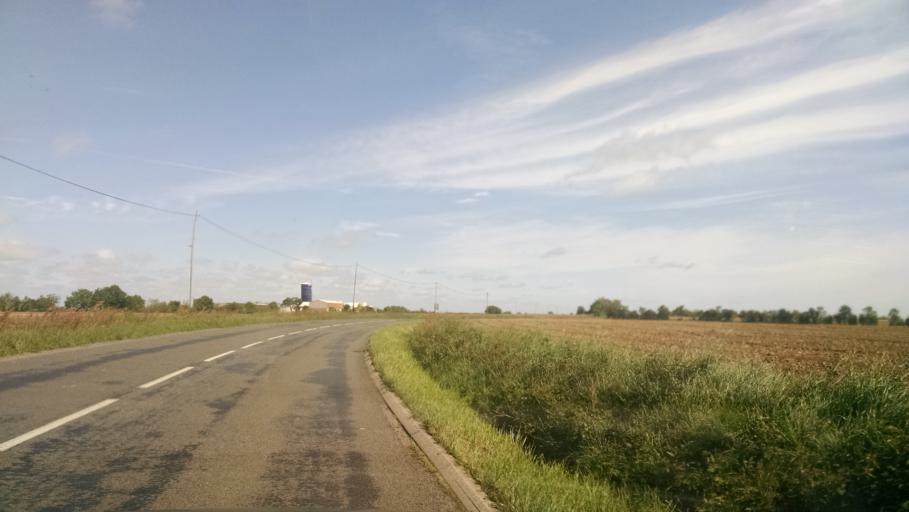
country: FR
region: Pays de la Loire
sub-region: Departement de la Loire-Atlantique
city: Saint-Hilaire-de-Clisson
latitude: 47.0404
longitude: -1.3251
